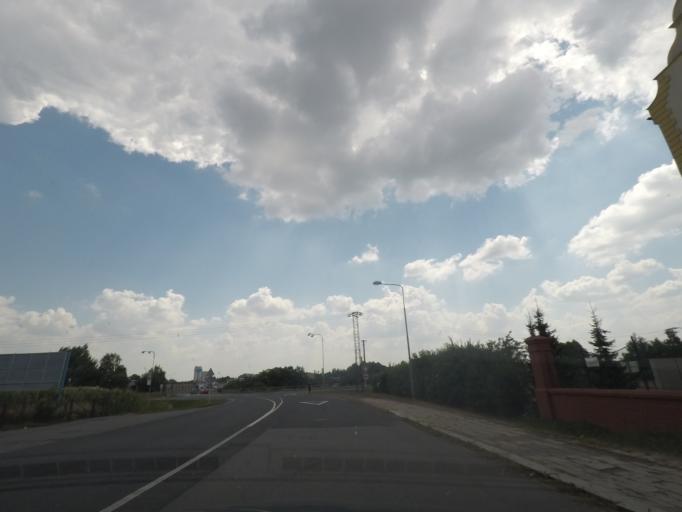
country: CZ
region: Olomoucky
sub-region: Okres Sumperk
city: Mohelnice
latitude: 49.7694
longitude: 16.9188
